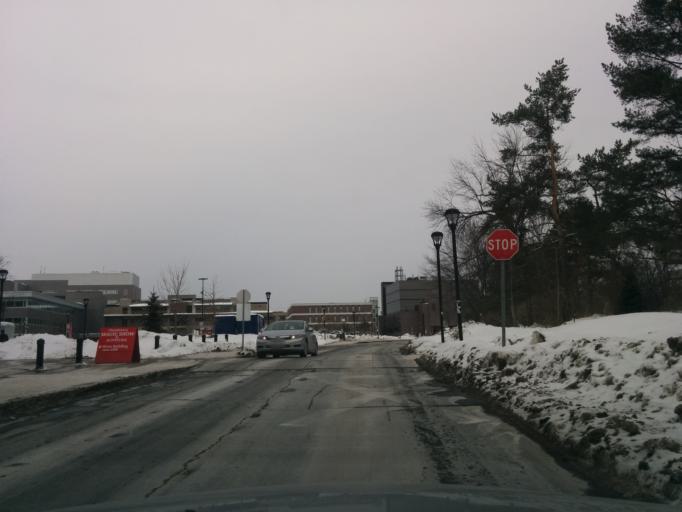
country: CA
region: Ontario
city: Ottawa
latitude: 45.3826
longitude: -75.6957
